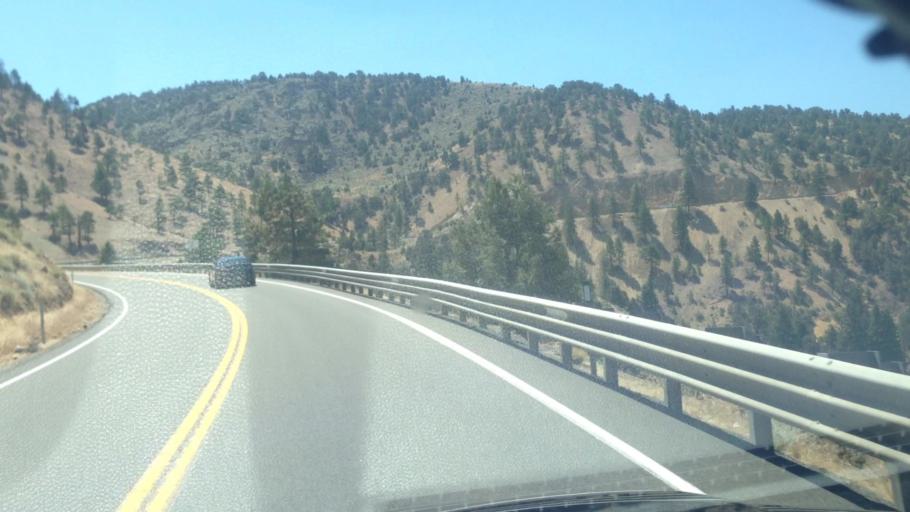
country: US
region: Nevada
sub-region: Storey County
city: Virginia City
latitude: 39.3872
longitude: -119.7063
